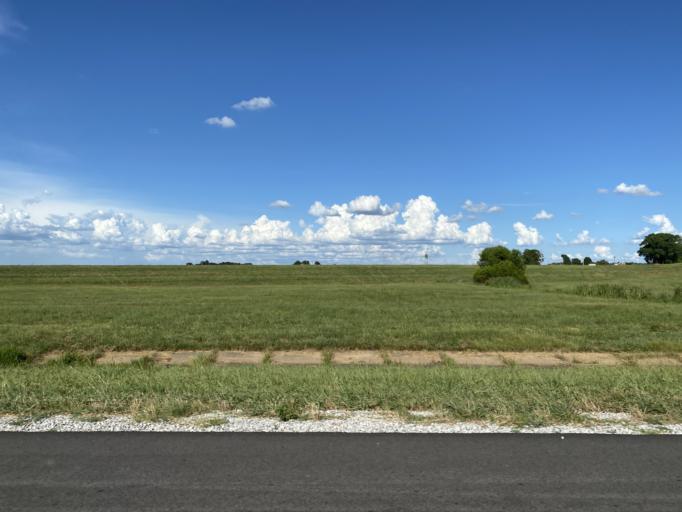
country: US
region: Alabama
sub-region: Limestone County
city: Athens
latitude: 34.7312
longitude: -86.9362
